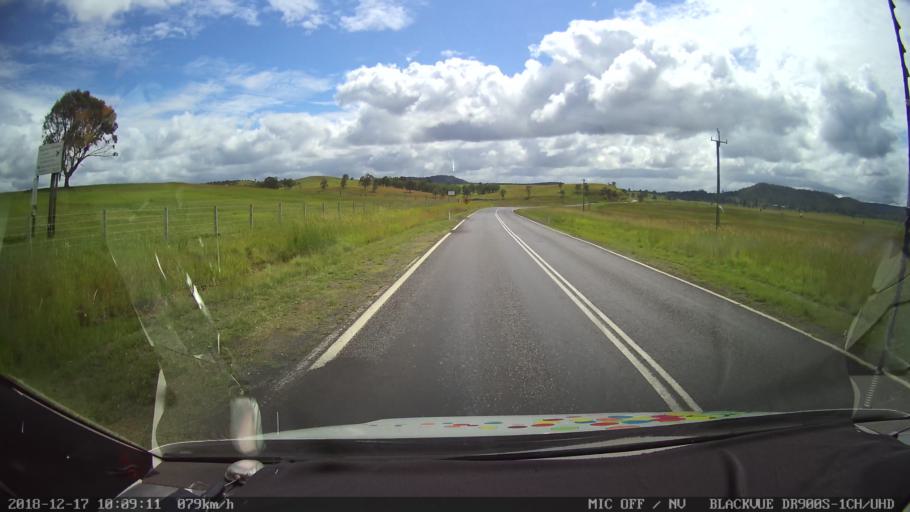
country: AU
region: New South Wales
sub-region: Tenterfield Municipality
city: Carrolls Creek
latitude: -28.8878
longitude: 152.5405
